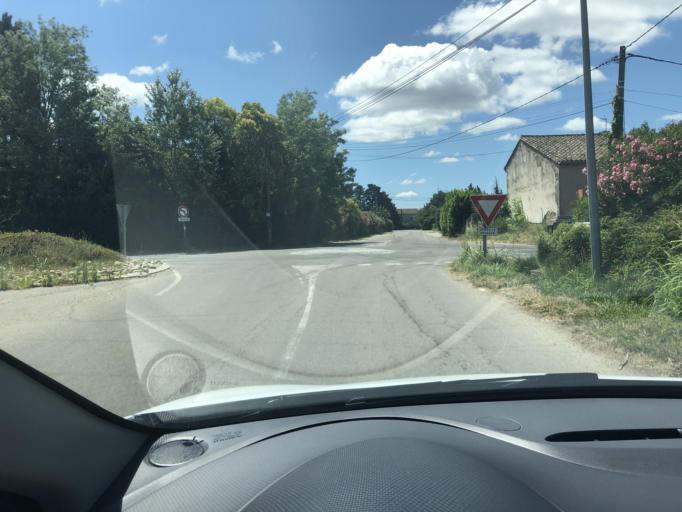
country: FR
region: Provence-Alpes-Cote d'Azur
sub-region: Departement des Bouches-du-Rhone
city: Chateaurenard
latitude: 43.8911
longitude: 4.8652
